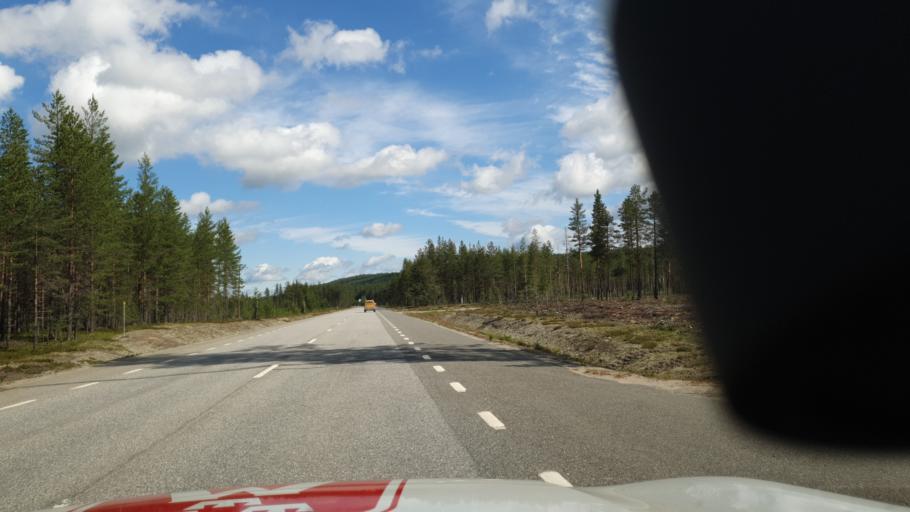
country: SE
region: Vaesterbotten
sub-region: Norsjo Kommun
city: Norsjoe
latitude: 64.5974
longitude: 19.2988
